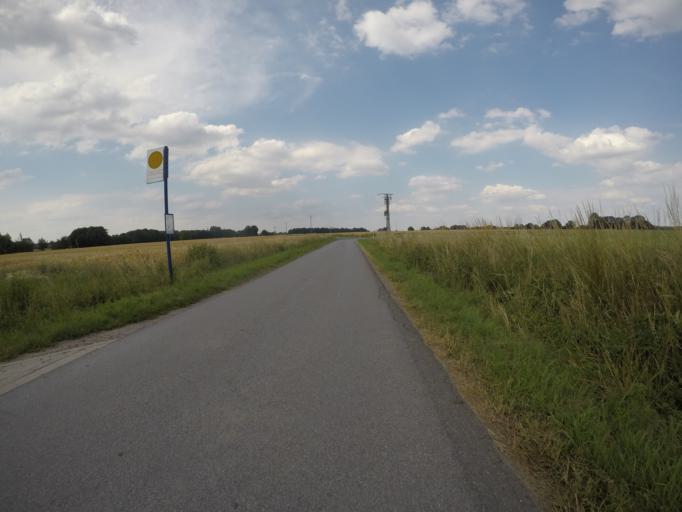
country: DE
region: North Rhine-Westphalia
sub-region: Regierungsbezirk Munster
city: Coesfeld
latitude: 51.8879
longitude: 7.0978
